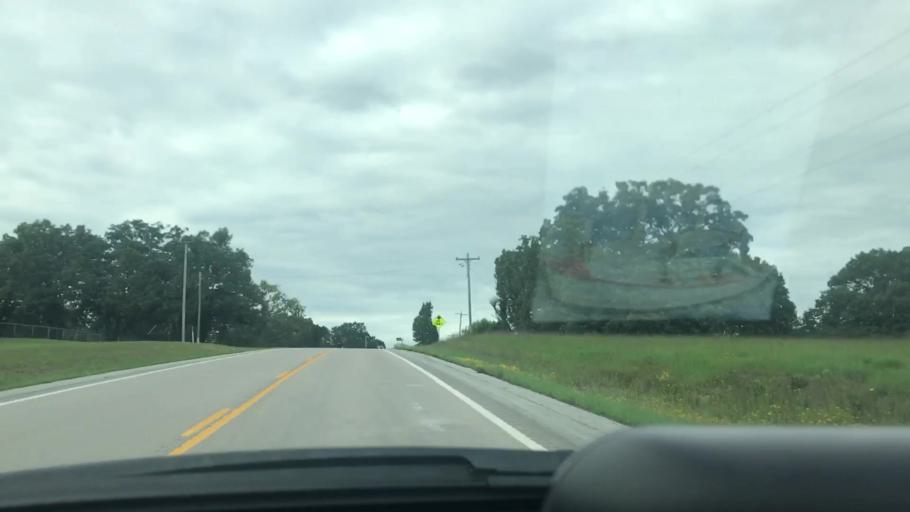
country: US
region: Missouri
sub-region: Benton County
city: Warsaw
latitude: 38.1528
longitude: -93.2953
